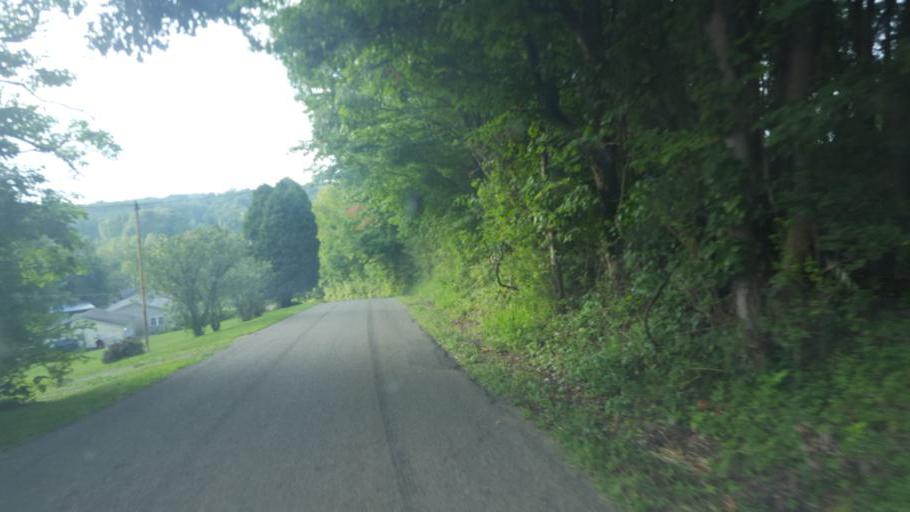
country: US
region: Ohio
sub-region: Sandusky County
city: Bellville
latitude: 40.6457
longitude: -82.4961
